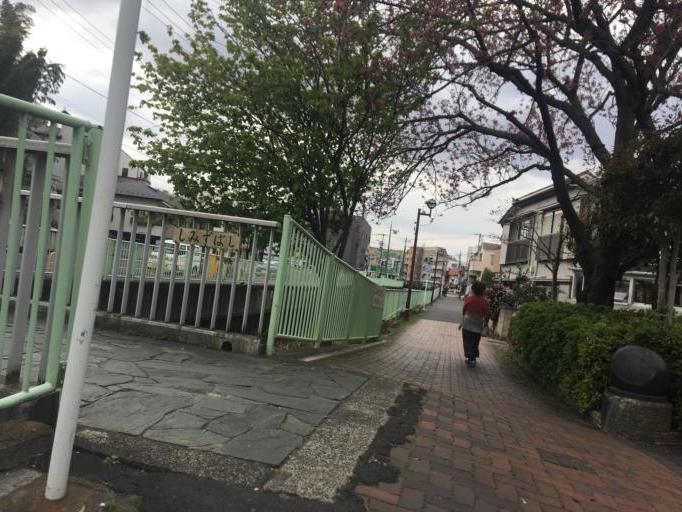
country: JP
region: Tokyo
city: Mitaka-shi
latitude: 35.6868
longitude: 139.6009
